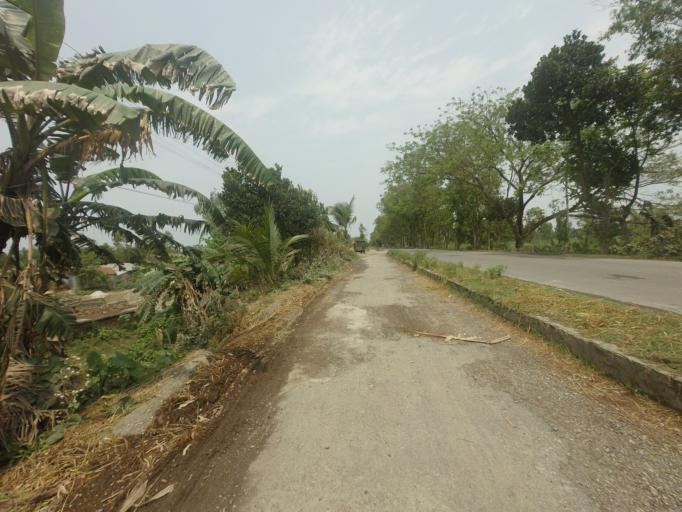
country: BD
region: Rajshahi
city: Sirajganj
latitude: 24.3365
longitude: 89.7005
